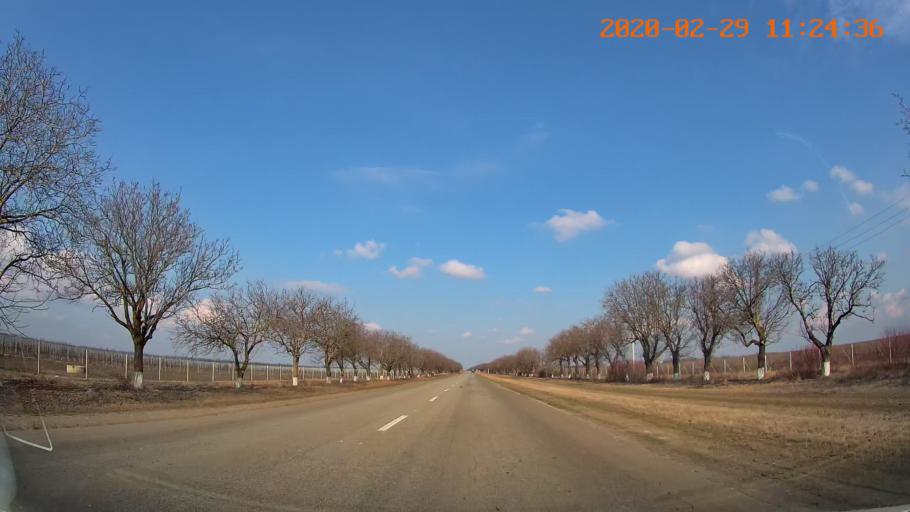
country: MD
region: Telenesti
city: Cocieri
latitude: 47.4263
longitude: 29.1539
